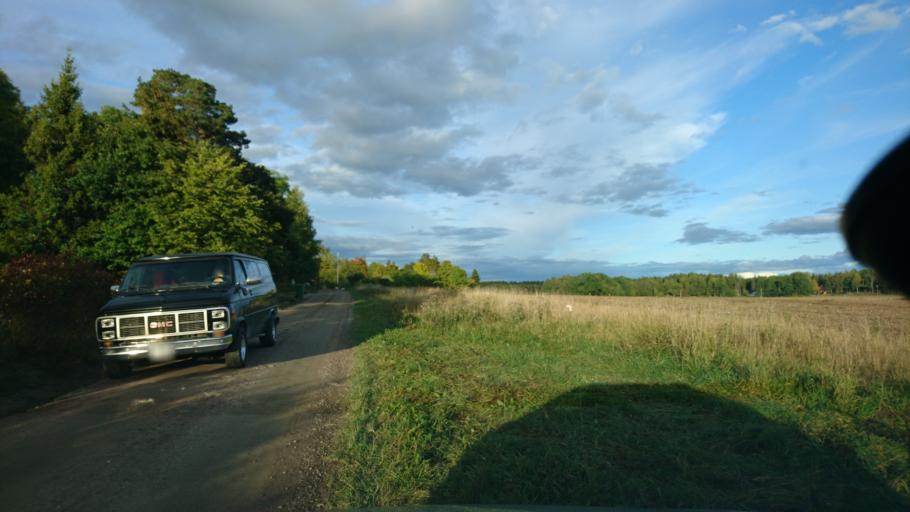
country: SE
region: Soedermanland
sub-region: Strangnas Kommun
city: Stallarholmen
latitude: 59.3756
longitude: 17.2184
